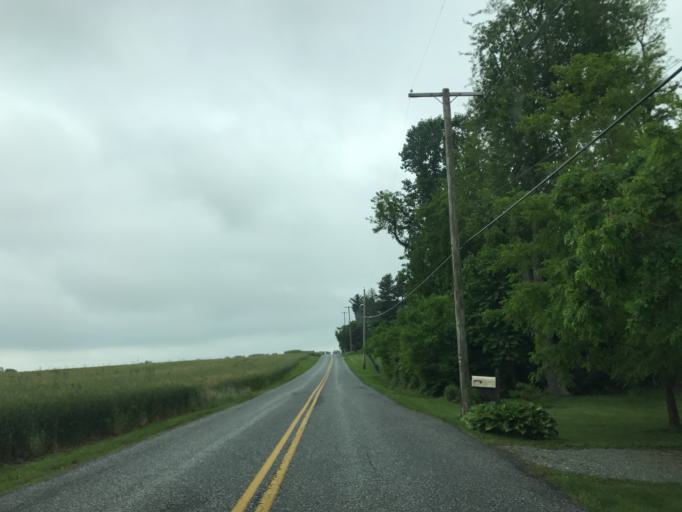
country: US
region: Pennsylvania
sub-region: York County
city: Susquehanna Trails
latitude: 39.7140
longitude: -76.4520
